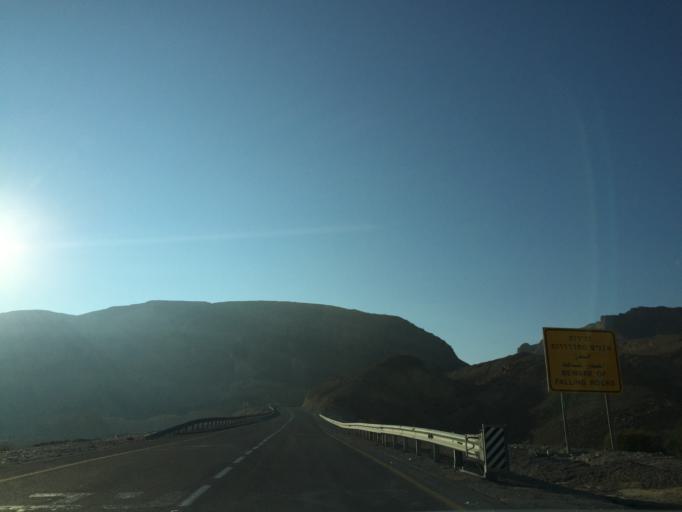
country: IL
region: Southern District
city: Mitzpe Ramon
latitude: 30.3244
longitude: 34.9558
